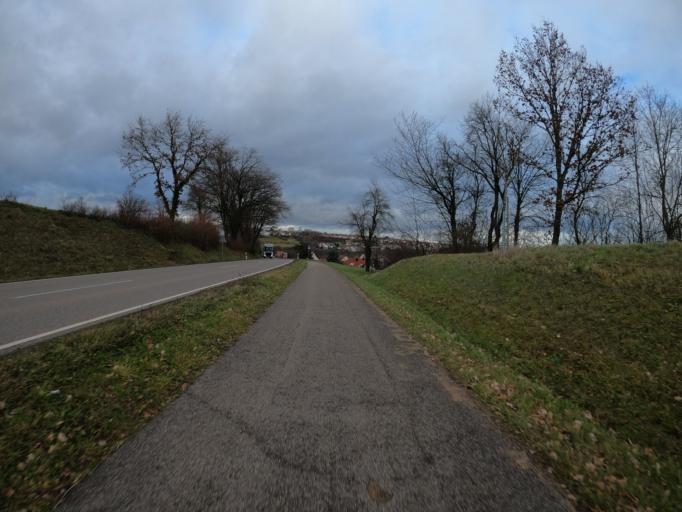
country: DE
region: Baden-Wuerttemberg
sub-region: Regierungsbezirk Stuttgart
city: Waldstetten
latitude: 48.7799
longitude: 9.8388
